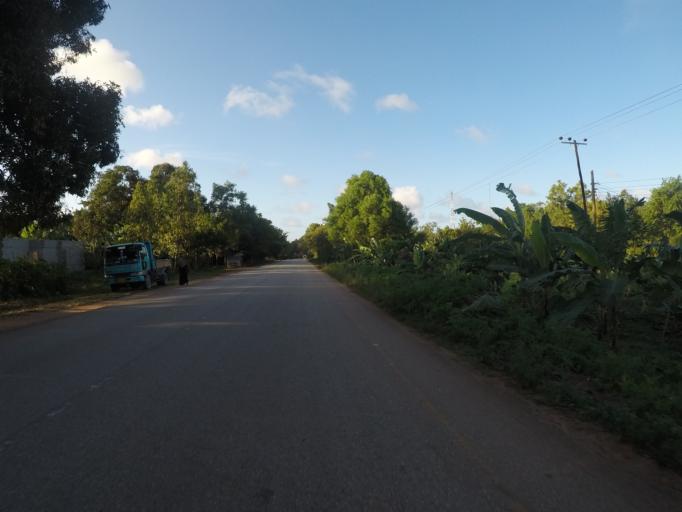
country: TZ
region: Zanzibar North
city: Kijini
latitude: -5.8102
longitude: 39.2945
